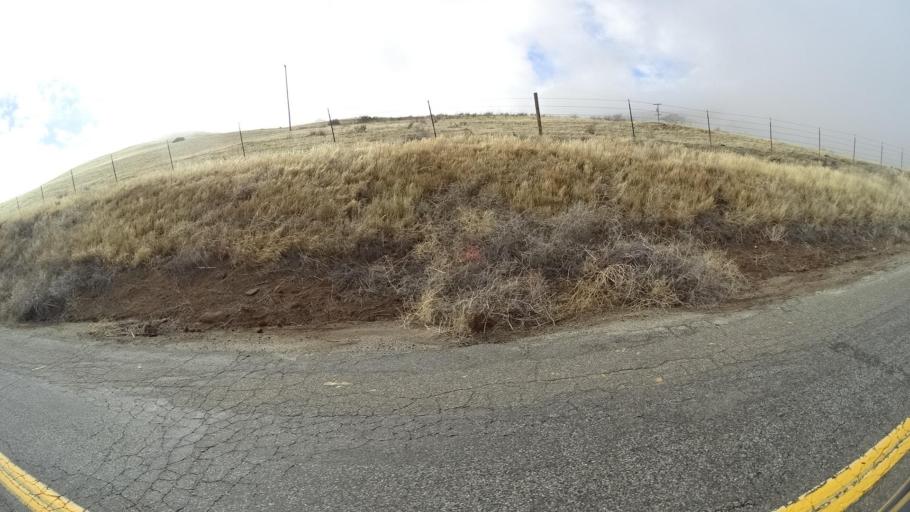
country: US
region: California
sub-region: Kern County
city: Maricopa
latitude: 34.9313
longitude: -119.4117
